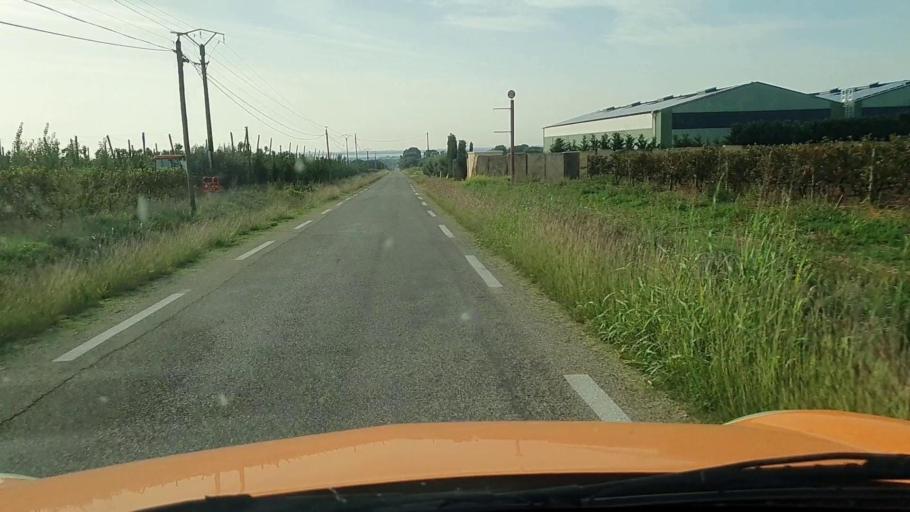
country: FR
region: Languedoc-Roussillon
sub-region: Departement du Gard
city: Beauvoisin
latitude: 43.6640
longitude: 4.3425
